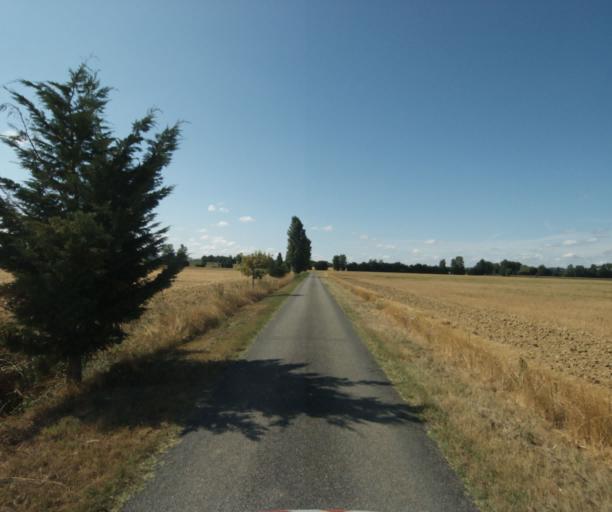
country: FR
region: Midi-Pyrenees
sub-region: Departement de la Haute-Garonne
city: Revel
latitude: 43.4947
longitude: 1.9867
